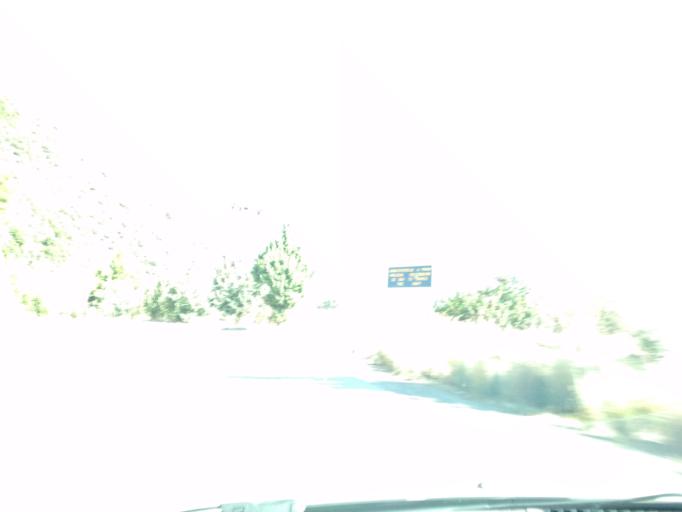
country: GR
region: Central Greece
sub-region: Nomos Evvoias
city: Oreoi
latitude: 38.8463
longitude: 23.0697
